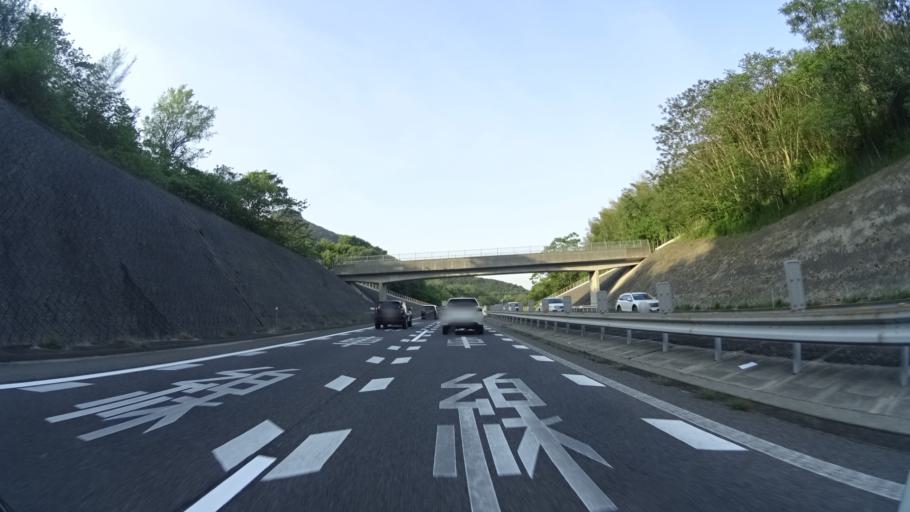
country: JP
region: Kagawa
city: Tadotsu
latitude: 34.2228
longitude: 133.7315
